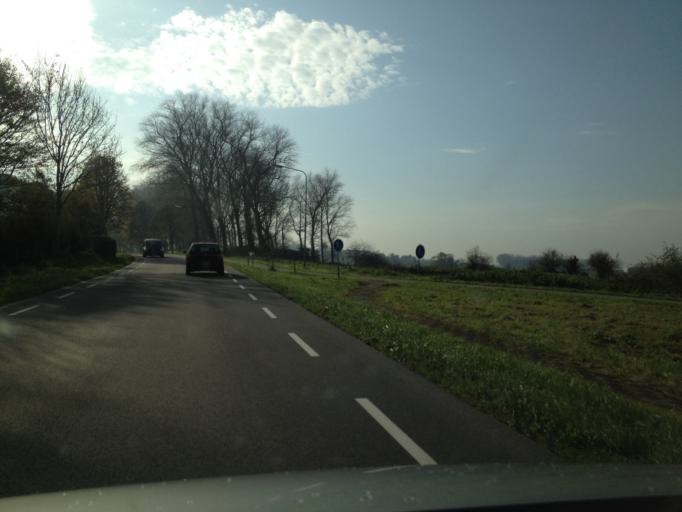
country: NL
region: Zeeland
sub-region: Gemeente Sluis
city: Sluis
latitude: 51.3162
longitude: 3.3905
